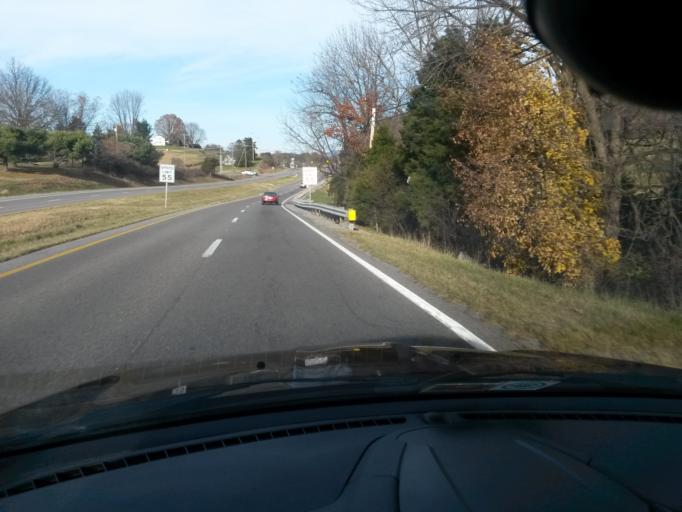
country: US
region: Virginia
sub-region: Botetourt County
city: Daleville
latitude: 37.4504
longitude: -79.8991
